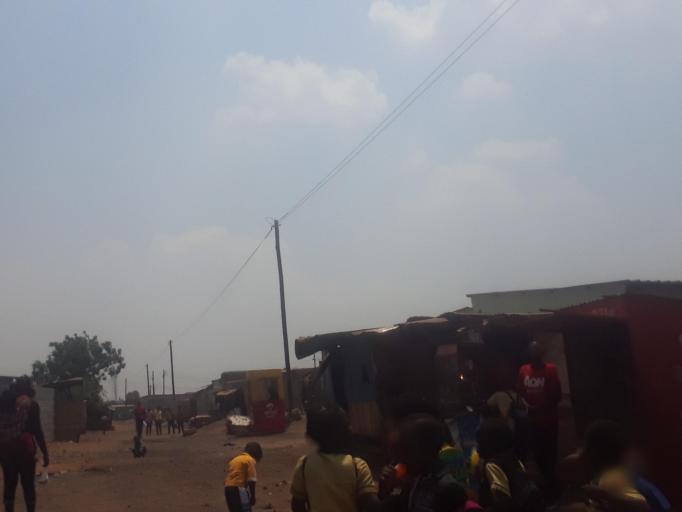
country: ZM
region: Lusaka
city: Lusaka
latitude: -15.3688
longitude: 28.2944
